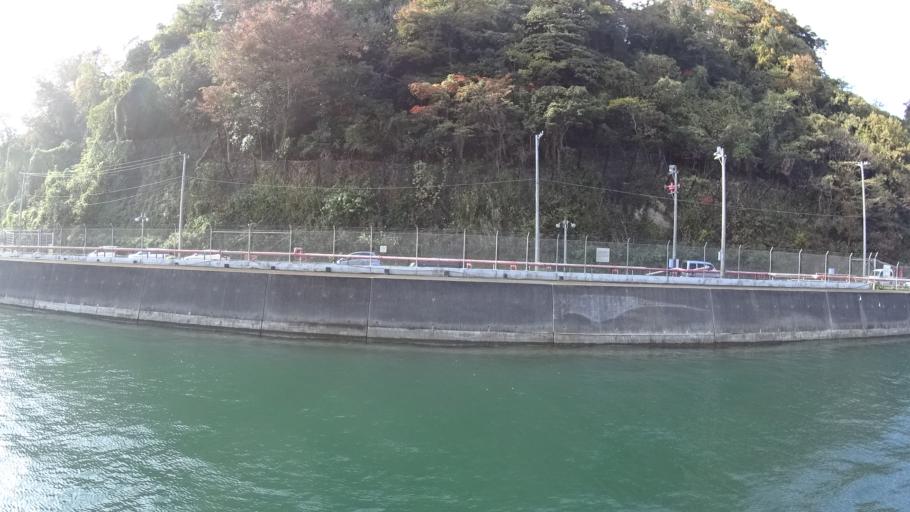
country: JP
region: Kanagawa
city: Yokosuka
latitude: 35.2960
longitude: 139.6467
